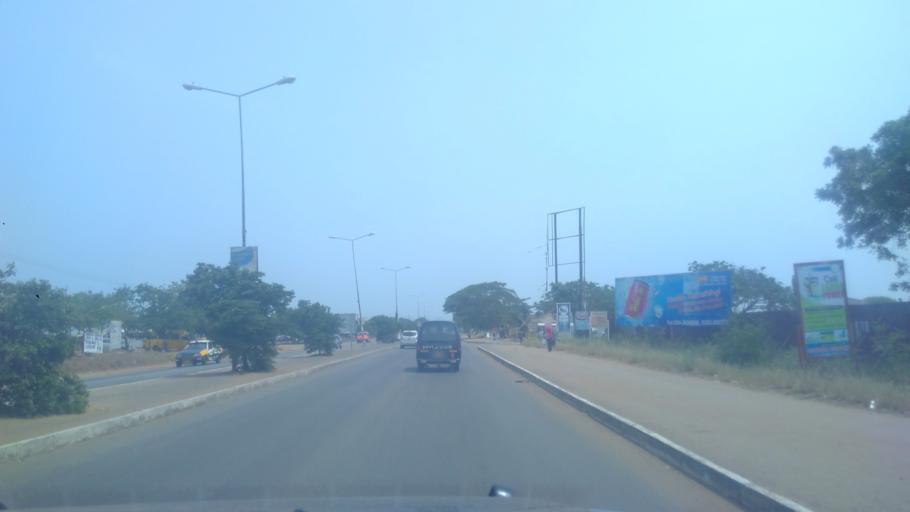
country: GH
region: Greater Accra
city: Tema
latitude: 5.6827
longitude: -0.0137
